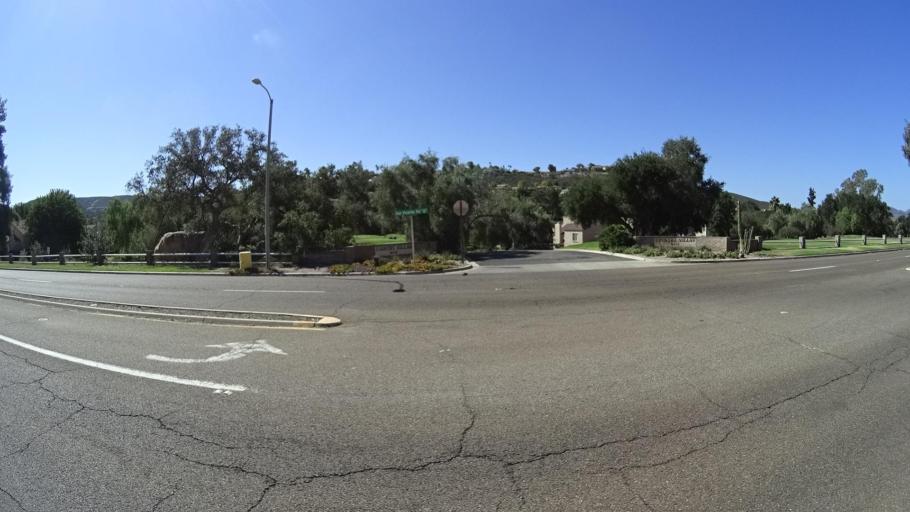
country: US
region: California
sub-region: San Diego County
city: San Diego Country Estates
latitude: 33.0057
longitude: -116.8151
